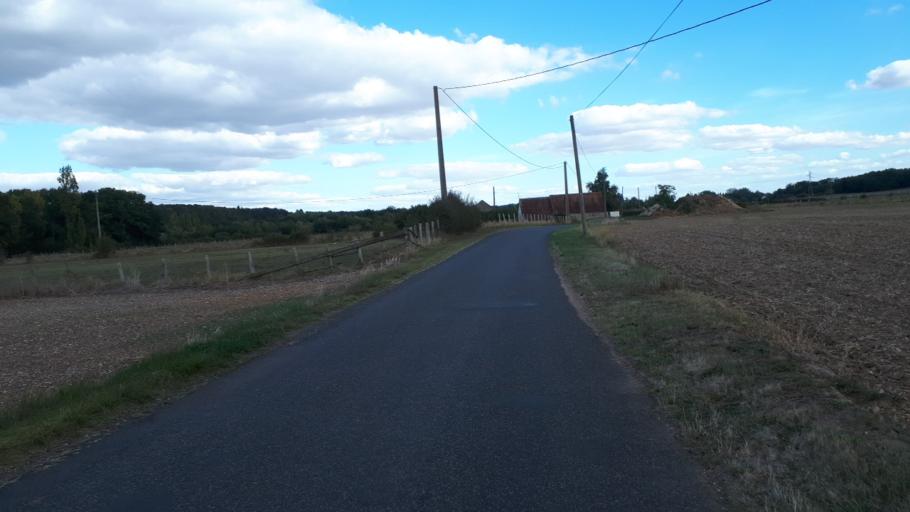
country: FR
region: Centre
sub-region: Departement du Loir-et-Cher
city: Villiers-sur-Loir
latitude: 47.8092
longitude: 0.9629
